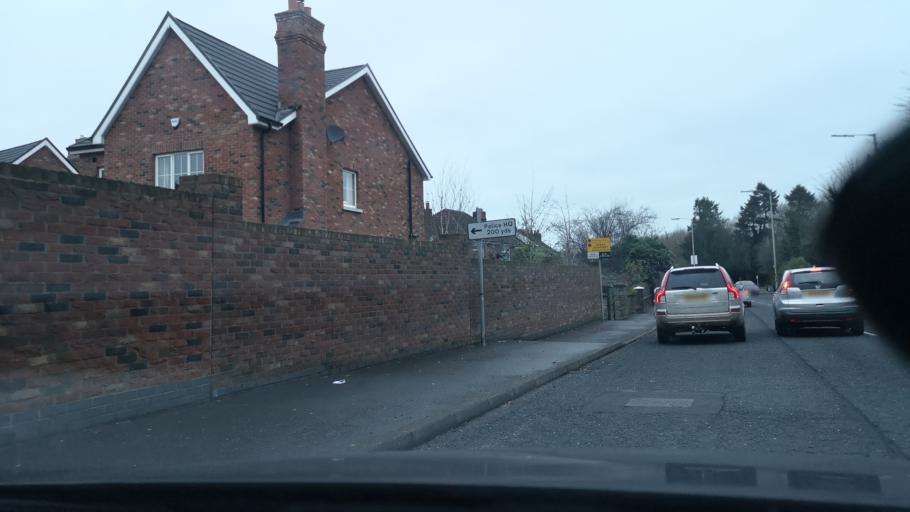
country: GB
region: Northern Ireland
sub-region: Castlereagh District
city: Castlereagh
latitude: 54.5882
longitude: -5.8567
